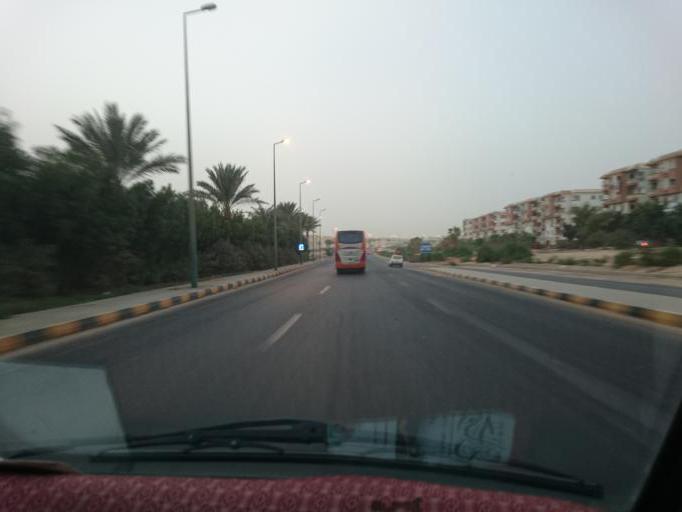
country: EG
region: Red Sea
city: Hurghada
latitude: 27.2108
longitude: 33.8192
